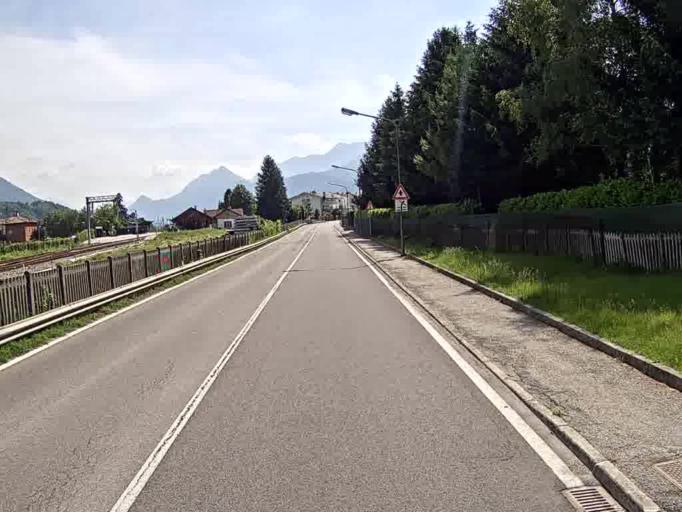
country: IT
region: Trentino-Alto Adige
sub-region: Provincia di Trento
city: Caldonazzo
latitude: 45.9970
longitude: 11.2623
